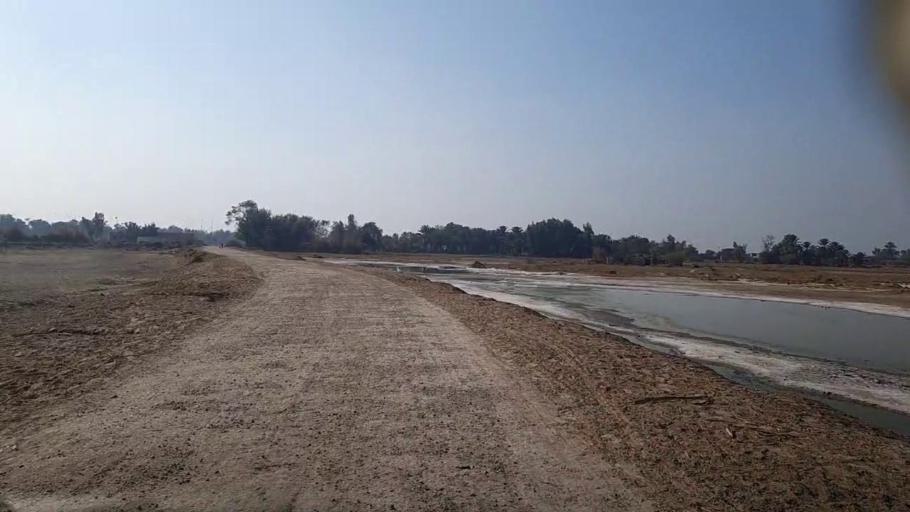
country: PK
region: Sindh
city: Mirpur Mathelo
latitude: 27.9006
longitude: 69.6425
